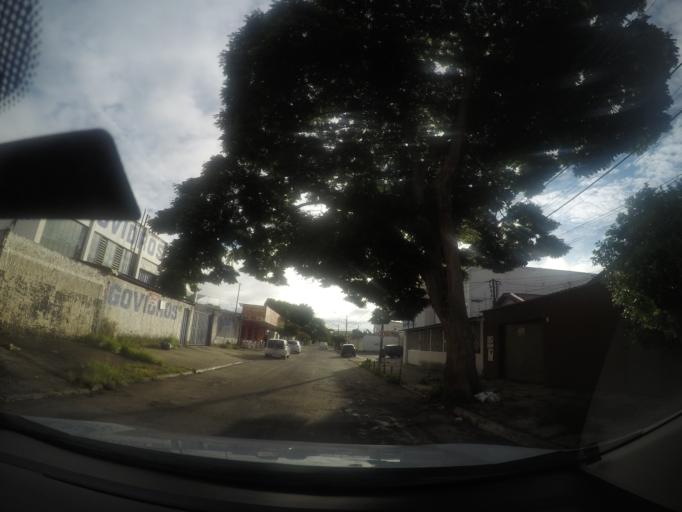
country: BR
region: Goias
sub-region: Goiania
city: Goiania
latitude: -16.6865
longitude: -49.3140
